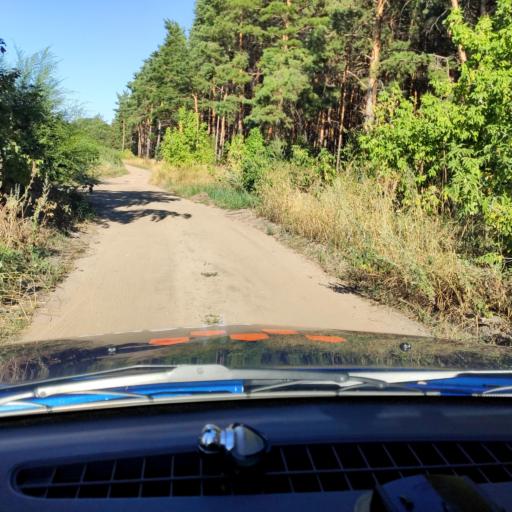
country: RU
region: Voronezj
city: Shilovo
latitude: 51.5404
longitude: 39.1629
